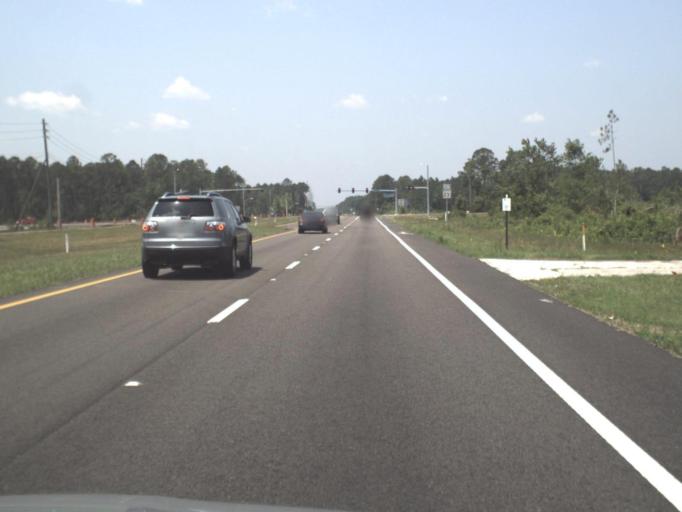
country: US
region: Florida
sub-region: Duval County
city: Baldwin
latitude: 30.2622
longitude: -81.8603
